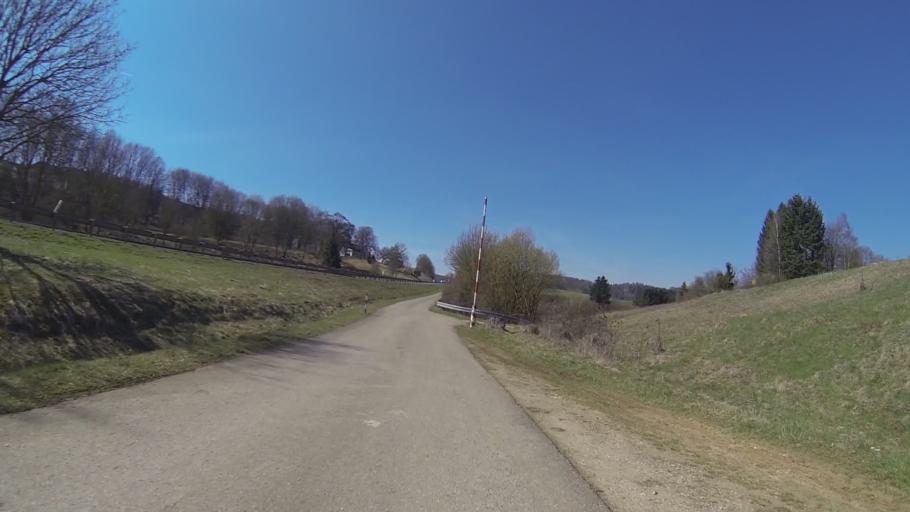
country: DE
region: Baden-Wuerttemberg
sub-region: Regierungsbezirk Stuttgart
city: Nattheim
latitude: 48.6931
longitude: 10.2274
